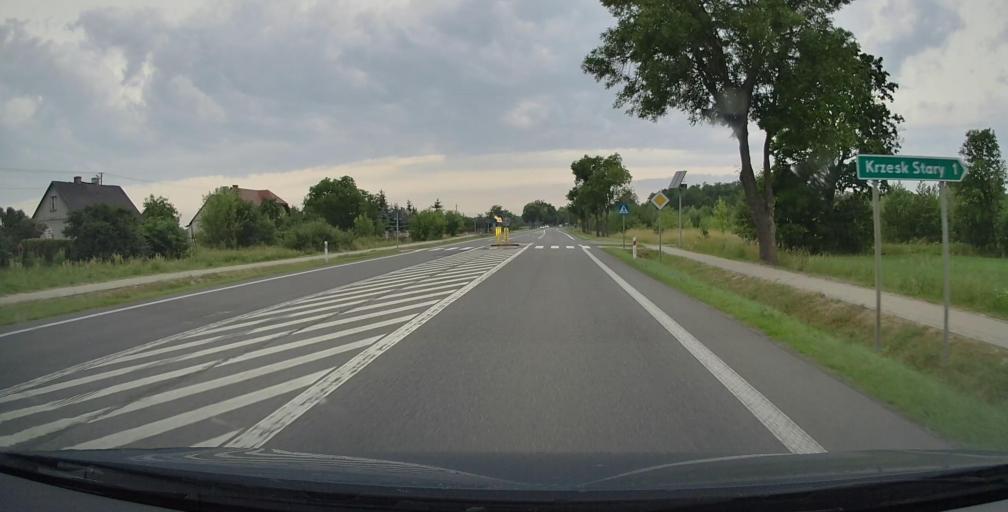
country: PL
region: Lublin Voivodeship
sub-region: Powiat lukowski
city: Trzebieszow
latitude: 52.0627
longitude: 22.5527
